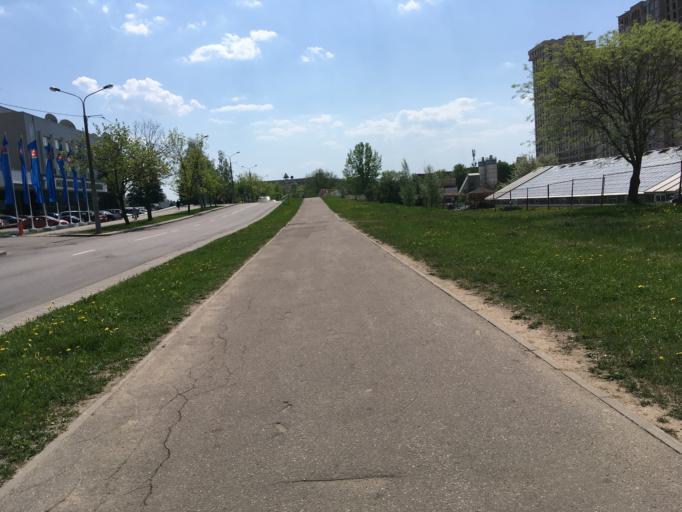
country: BY
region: Minsk
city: Minsk
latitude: 53.9244
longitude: 27.6280
